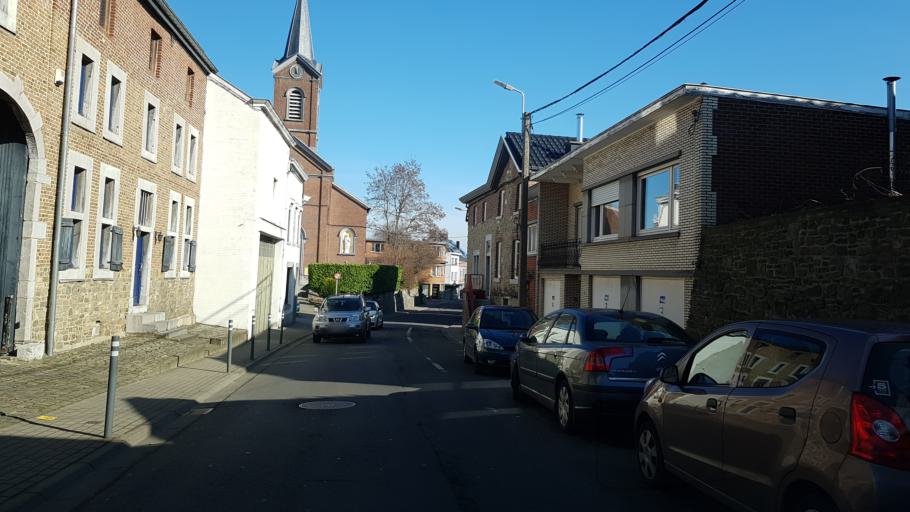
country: BE
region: Wallonia
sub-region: Province de Liege
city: Oupeye
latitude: 50.6971
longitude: 5.6520
